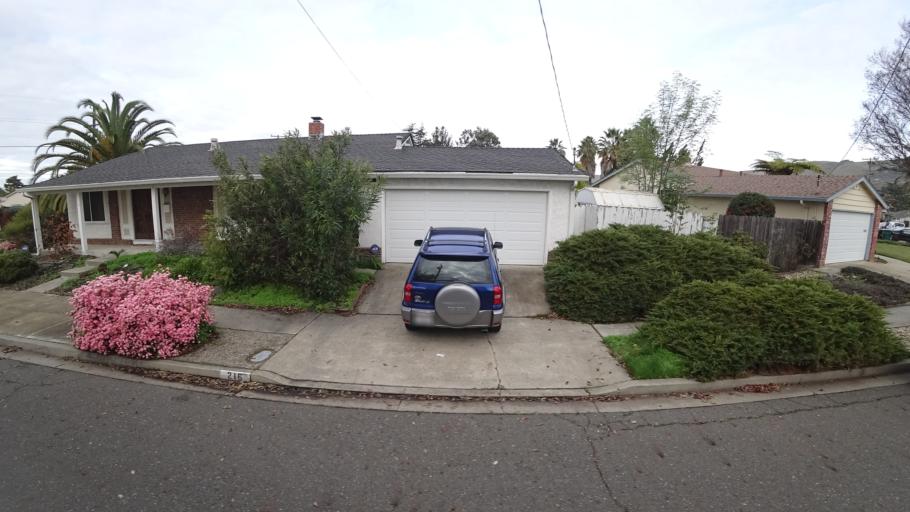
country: US
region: California
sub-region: Alameda County
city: Union City
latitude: 37.6202
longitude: -122.0425
